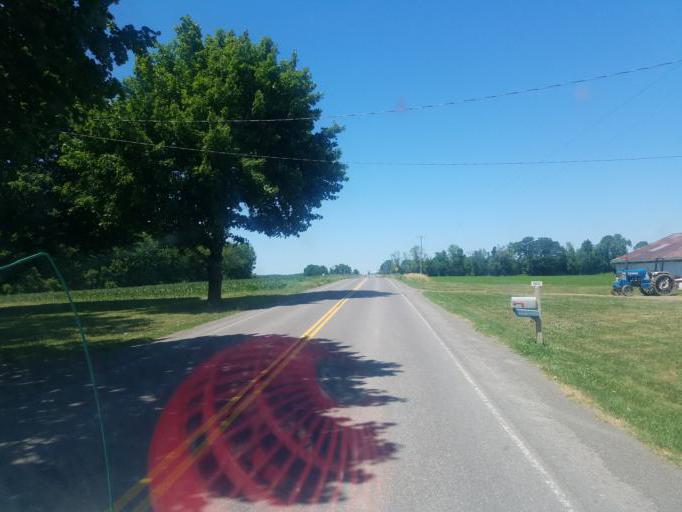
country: US
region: New York
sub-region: Yates County
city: Penn Yan
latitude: 42.7154
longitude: -76.9974
